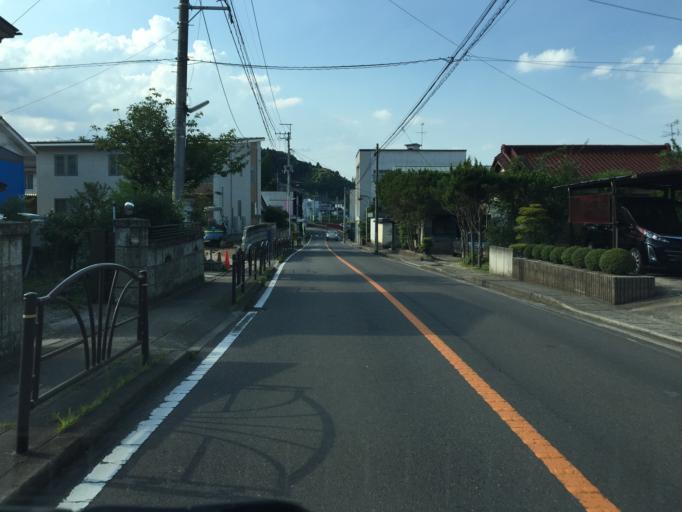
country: JP
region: Fukushima
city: Nihommatsu
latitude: 37.5597
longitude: 140.4128
